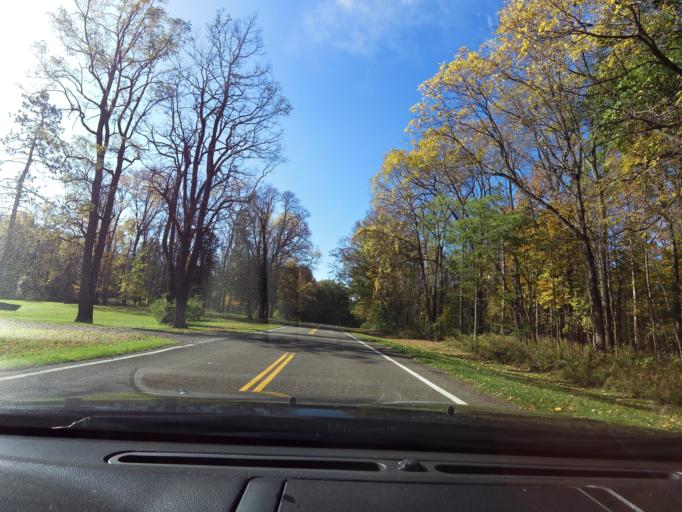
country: US
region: New York
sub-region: Livingston County
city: Mount Morris
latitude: 42.7153
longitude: -77.9313
